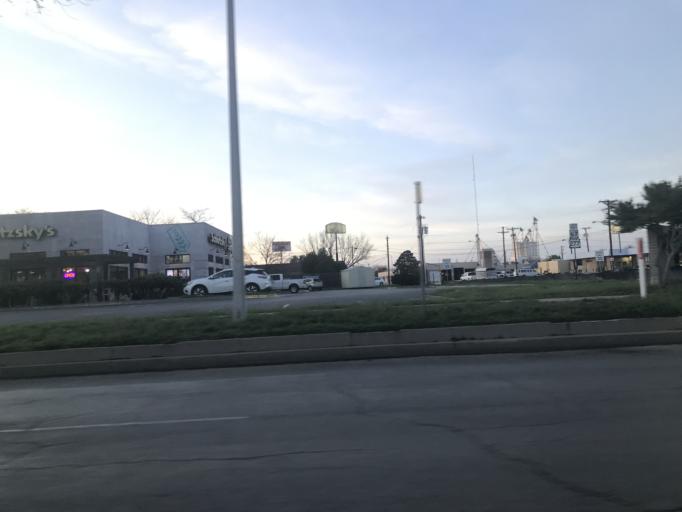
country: US
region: Texas
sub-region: Tom Green County
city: San Angelo
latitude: 31.4621
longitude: -100.4430
